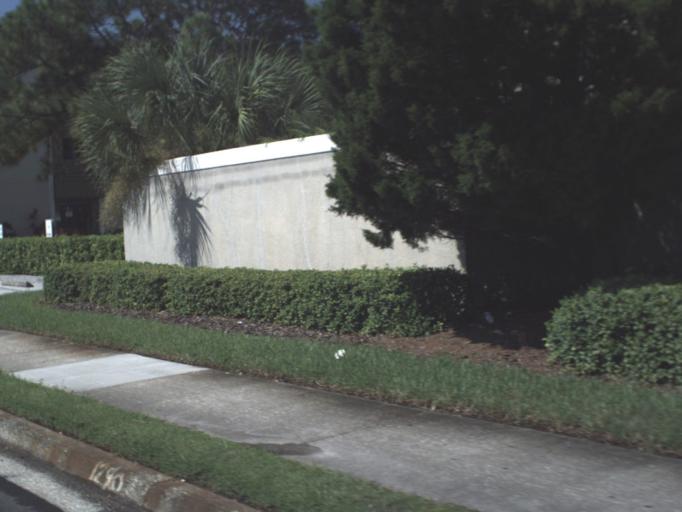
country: US
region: Florida
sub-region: Pinellas County
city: Pinellas Park
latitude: 27.8441
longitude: -82.7287
